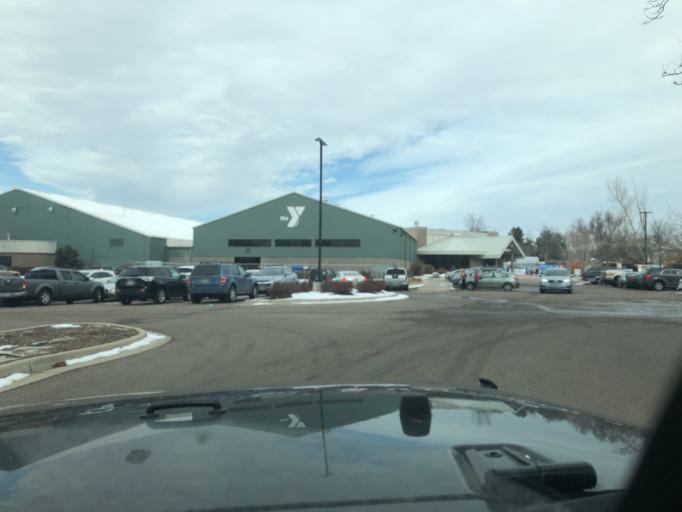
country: US
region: Colorado
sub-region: Boulder County
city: Longmont
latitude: 40.1740
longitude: -105.0869
